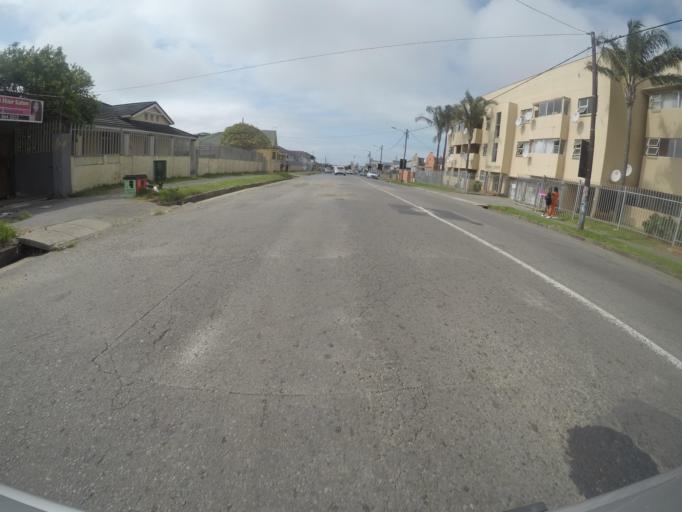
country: ZA
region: Eastern Cape
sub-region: Buffalo City Metropolitan Municipality
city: East London
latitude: -33.0006
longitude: 27.9052
